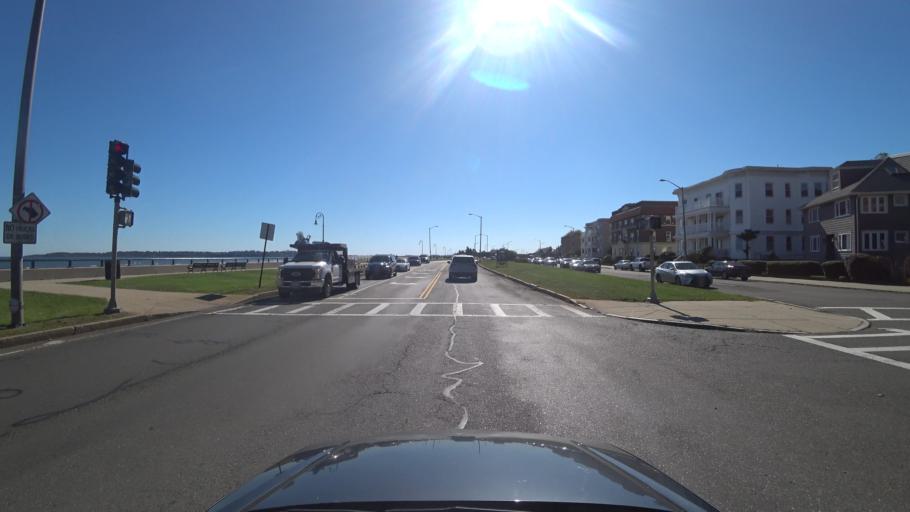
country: US
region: Massachusetts
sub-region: Essex County
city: Lynn
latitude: 42.4589
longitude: -70.9346
